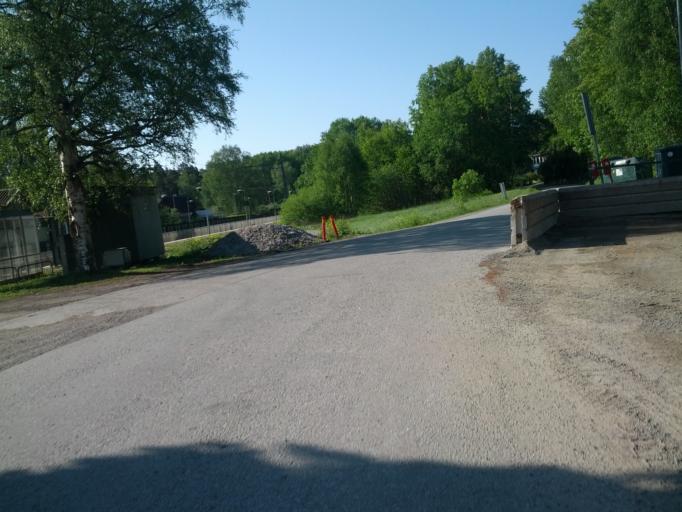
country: SE
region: Stockholm
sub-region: Taby Kommun
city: Taby
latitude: 59.4260
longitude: 18.0509
